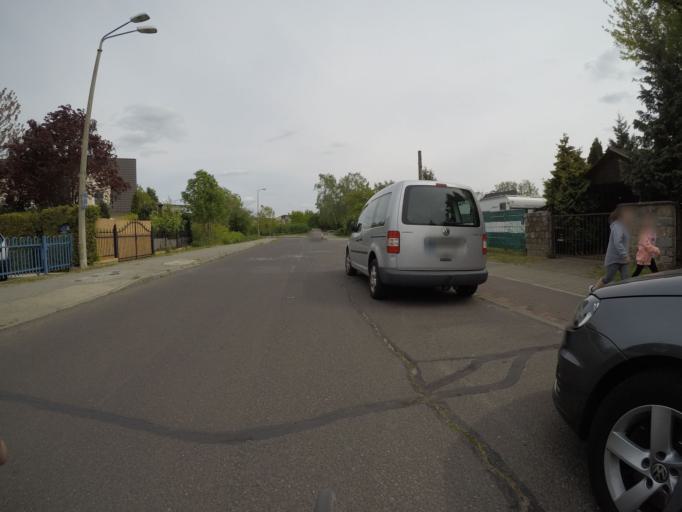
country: DE
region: Berlin
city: Altglienicke
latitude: 52.4040
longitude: 13.5368
